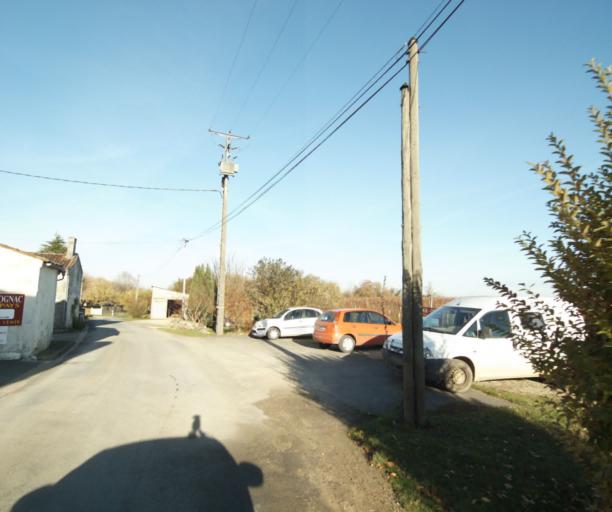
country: FR
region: Poitou-Charentes
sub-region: Departement de la Charente-Maritime
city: Burie
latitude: 45.7783
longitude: -0.4198
